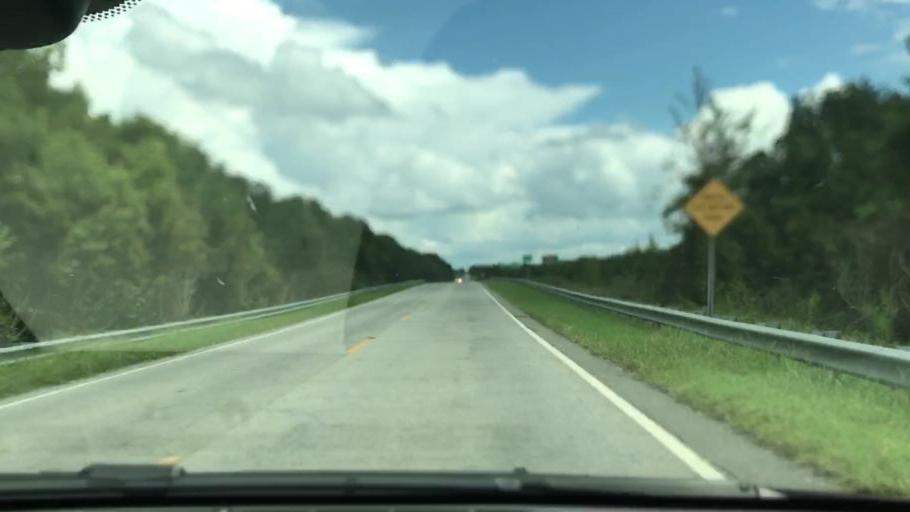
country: US
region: Georgia
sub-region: Seminole County
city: Donalsonville
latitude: 30.9783
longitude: -84.9999
